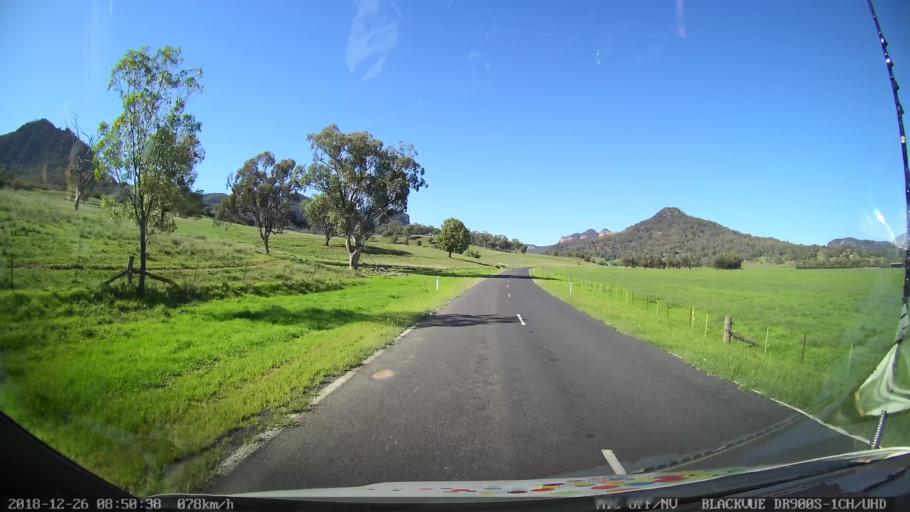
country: AU
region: New South Wales
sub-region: Mid-Western Regional
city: Kandos
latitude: -32.5777
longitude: 150.0941
